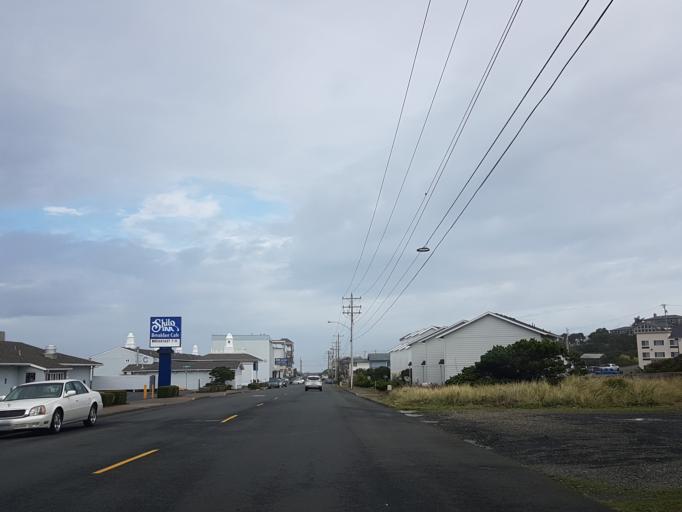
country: US
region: Oregon
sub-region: Lincoln County
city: Newport
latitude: 44.6311
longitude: -124.0633
